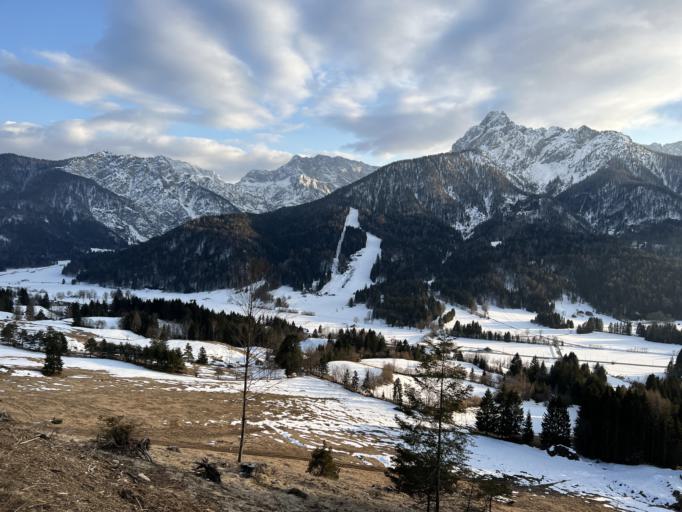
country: AT
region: Carinthia
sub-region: Politischer Bezirk Villach Land
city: Arnoldstein
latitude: 46.5046
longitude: 13.7032
